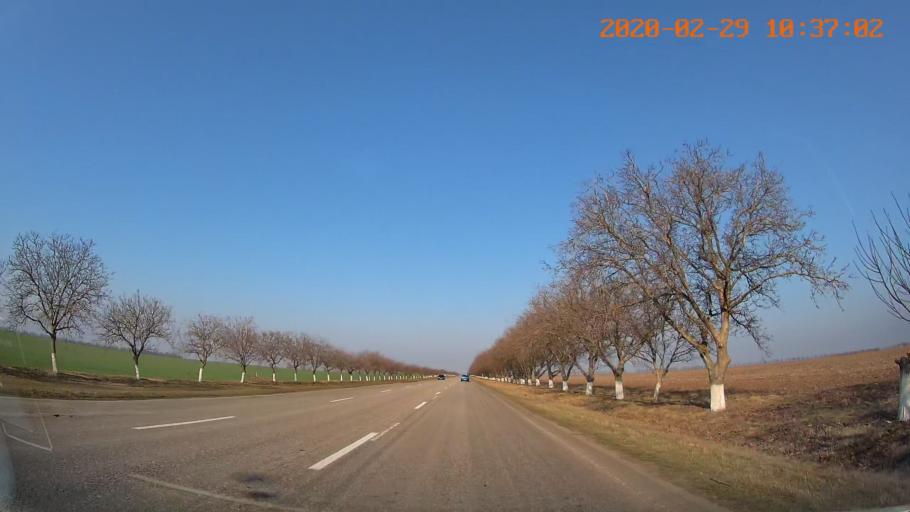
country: MD
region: Anenii Noi
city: Varnita
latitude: 47.0016
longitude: 29.4962
